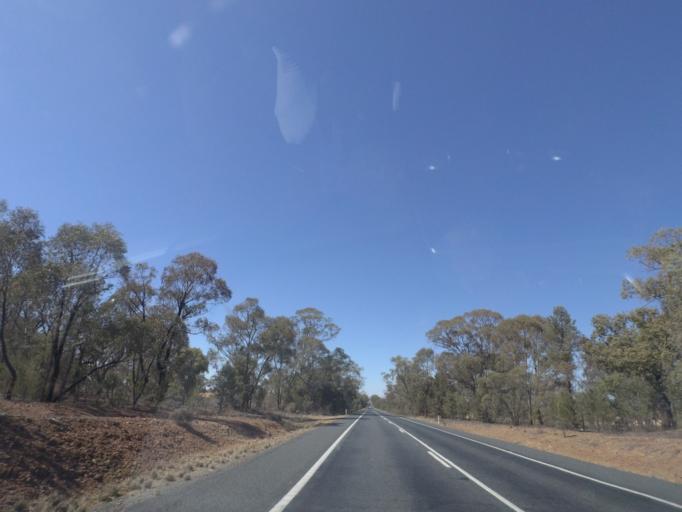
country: AU
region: New South Wales
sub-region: Bland
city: West Wyalong
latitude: -34.1680
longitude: 147.1156
